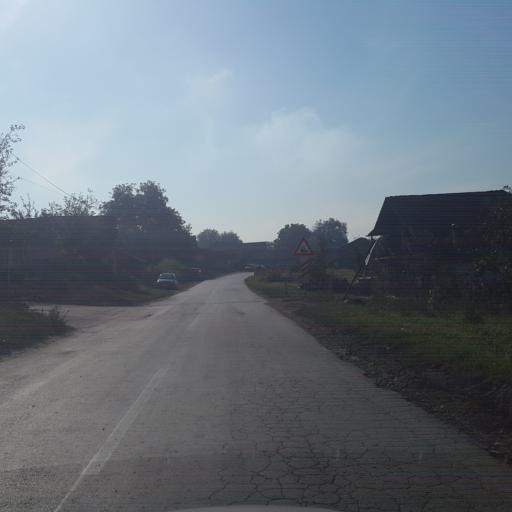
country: RS
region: Central Serbia
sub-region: Pirotski Okrug
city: Pirot
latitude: 43.1864
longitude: 22.5720
